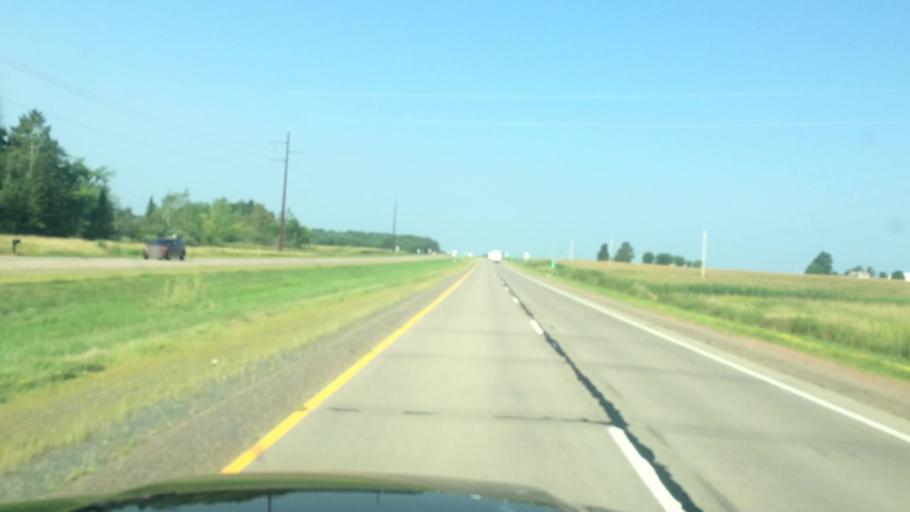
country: US
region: Wisconsin
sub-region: Marathon County
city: Edgar
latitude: 44.9444
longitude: -90.0182
